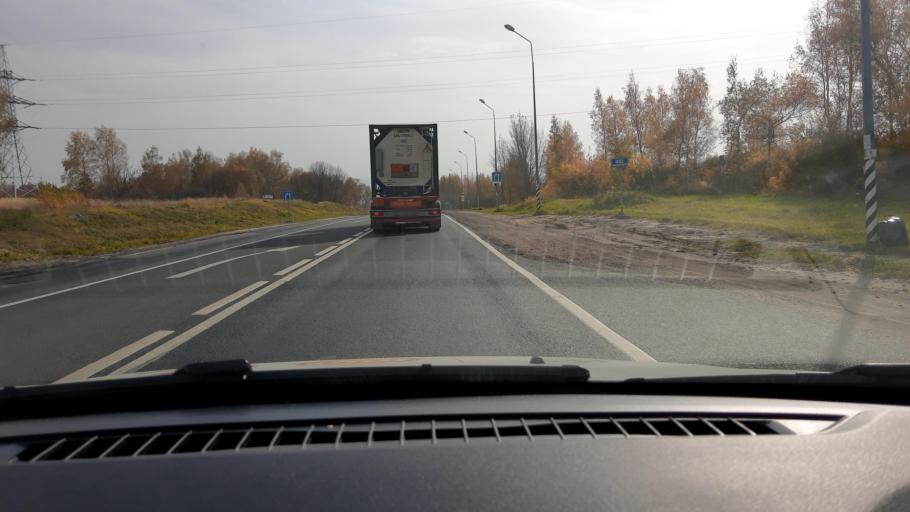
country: RU
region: Nizjnij Novgorod
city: Kstovo
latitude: 56.1096
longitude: 44.2850
